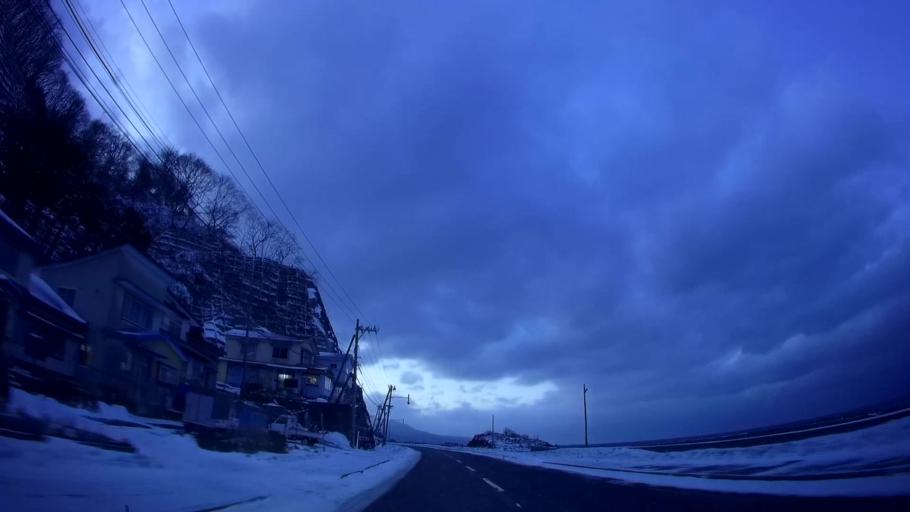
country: JP
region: Hokkaido
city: Hakodate
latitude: 41.8889
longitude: 141.0612
